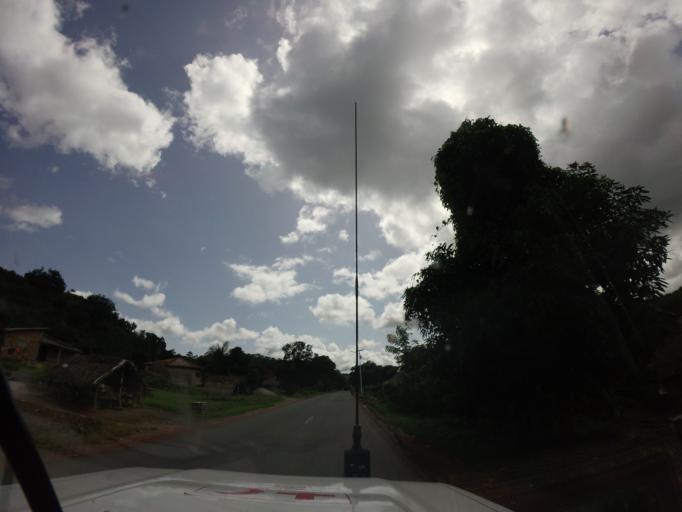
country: GN
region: Mamou
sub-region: Mamou Prefecture
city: Mamou
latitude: 10.2900
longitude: -11.9826
